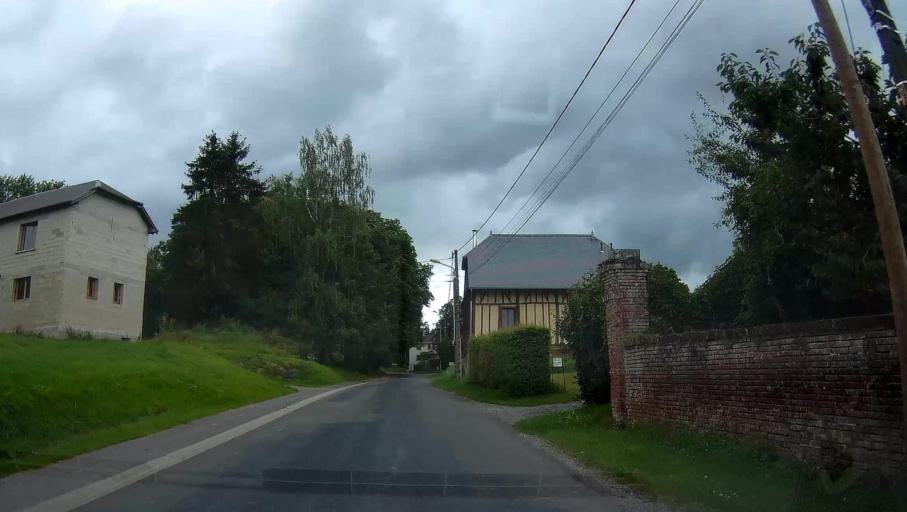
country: FR
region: Picardie
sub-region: Departement de l'Aisne
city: Rozoy-sur-Serre
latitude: 49.6916
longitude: 4.2458
